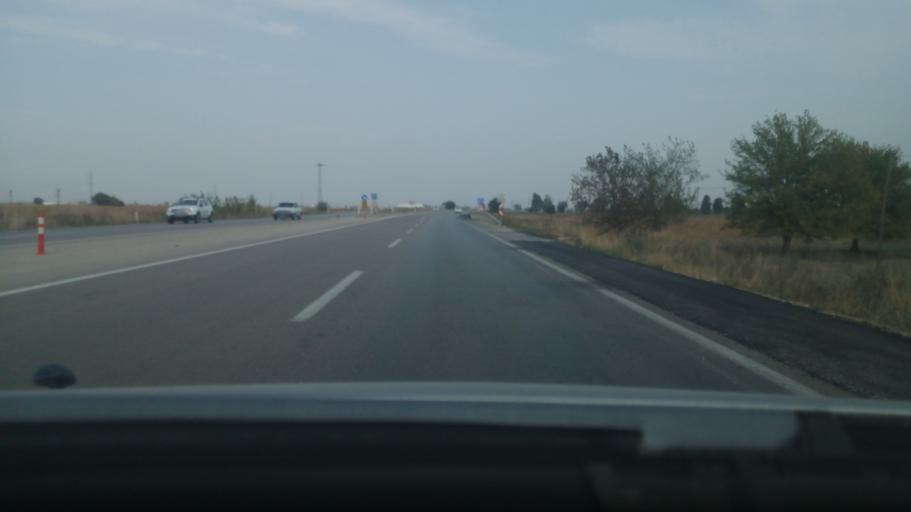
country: TR
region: Adana
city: Imamoglu
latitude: 37.2803
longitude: 35.6928
